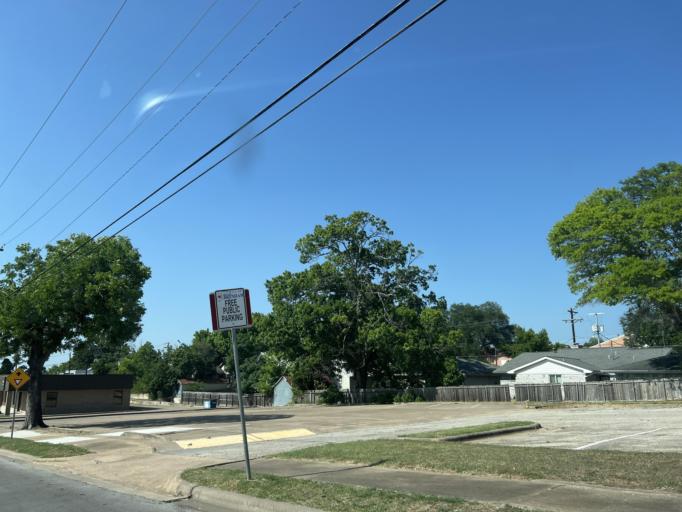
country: US
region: Texas
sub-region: Washington County
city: Brenham
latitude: 30.1691
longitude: -96.3986
